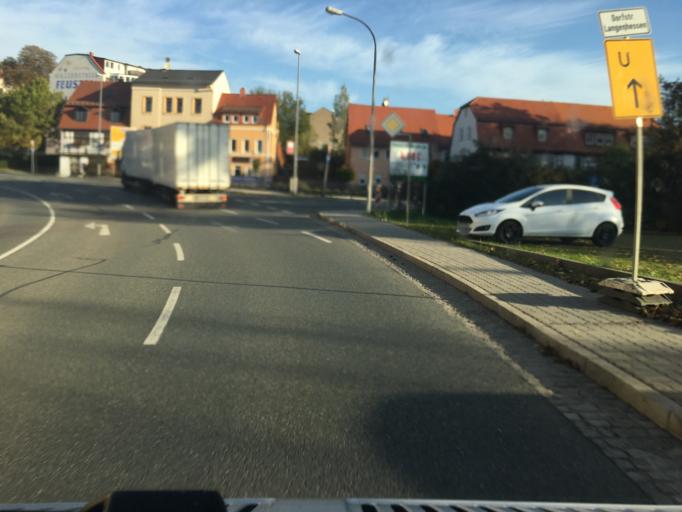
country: DE
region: Saxony
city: Werdau
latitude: 50.7391
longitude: 12.3772
